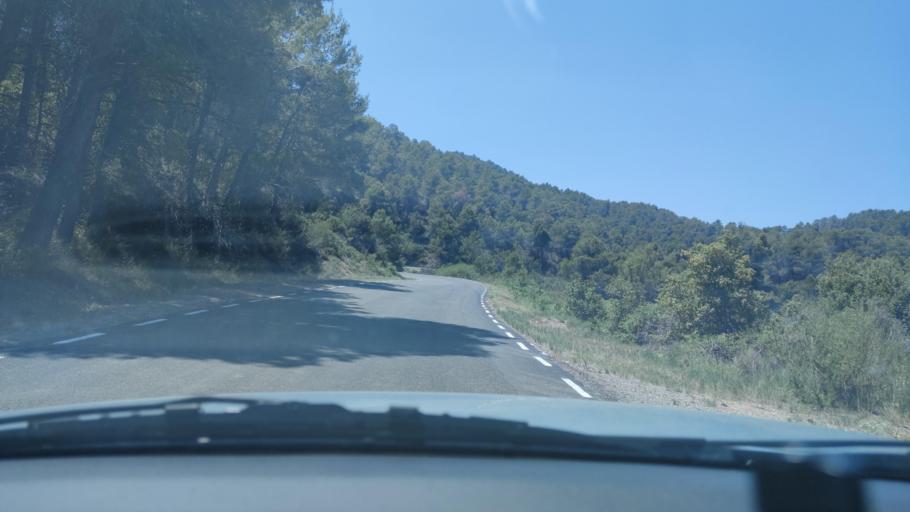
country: ES
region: Catalonia
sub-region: Provincia de Tarragona
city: Ulldemolins
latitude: 41.3484
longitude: 0.8855
